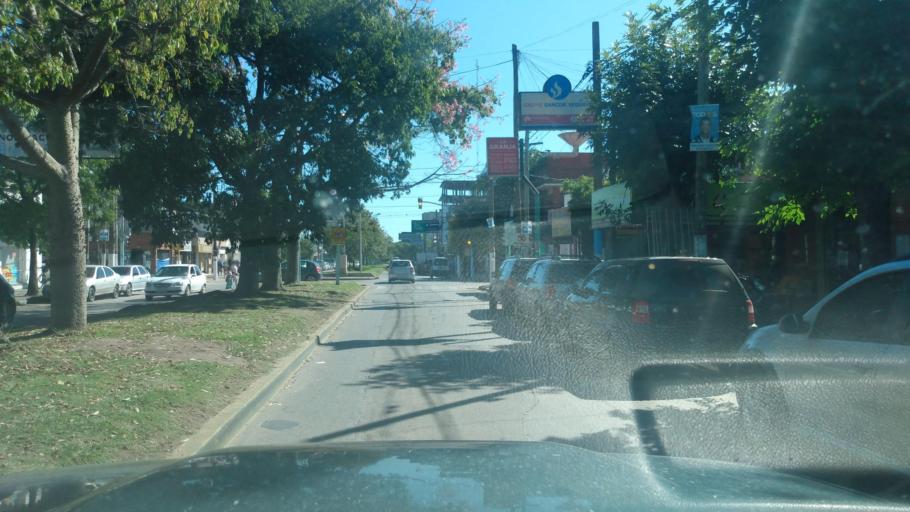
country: AR
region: Buenos Aires
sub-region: Partido de General Rodriguez
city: General Rodriguez
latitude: -34.6068
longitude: -58.9506
